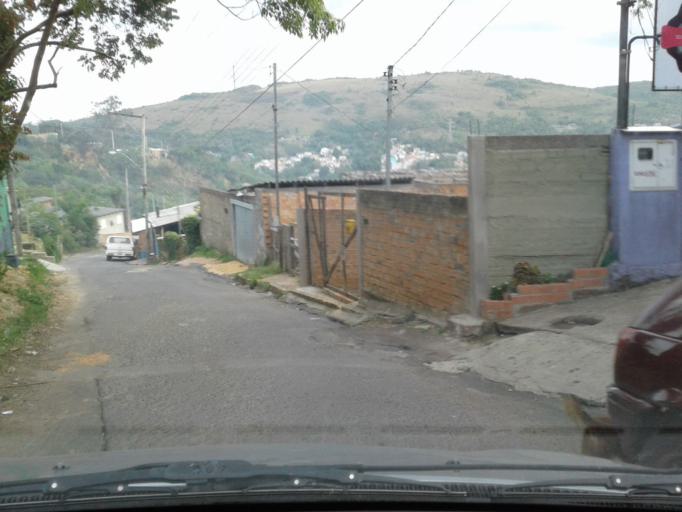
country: BR
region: Rio Grande do Sul
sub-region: Porto Alegre
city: Porto Alegre
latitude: -30.0627
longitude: -51.1460
